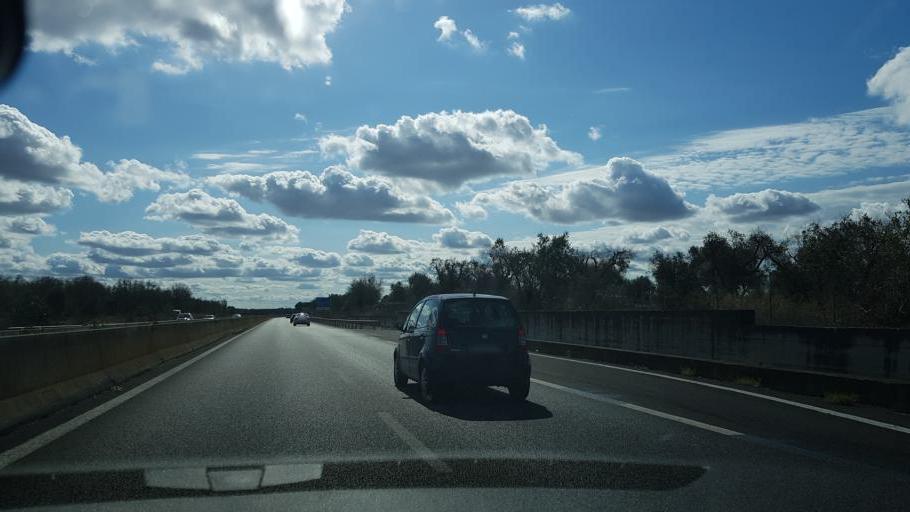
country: IT
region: Apulia
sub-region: Provincia di Lecce
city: Squinzano
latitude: 40.4479
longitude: 18.0710
